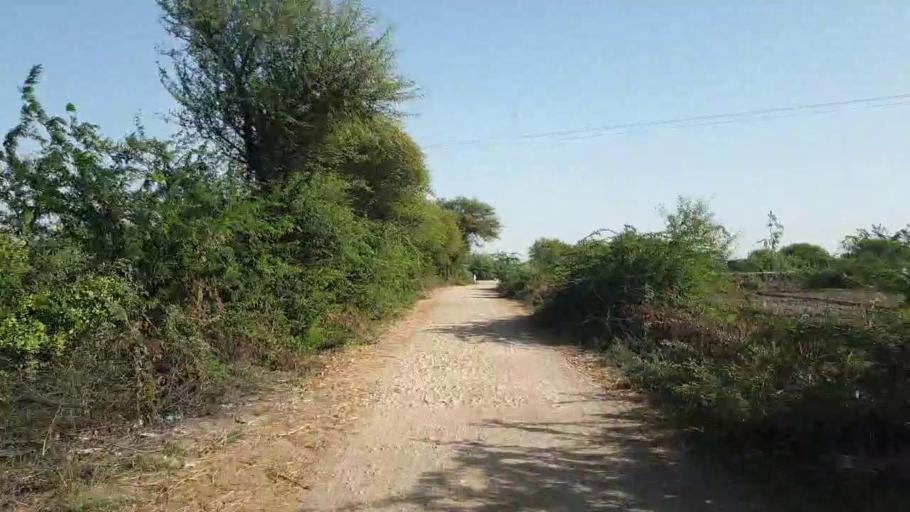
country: PK
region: Sindh
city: Badin
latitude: 24.6016
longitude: 68.9147
